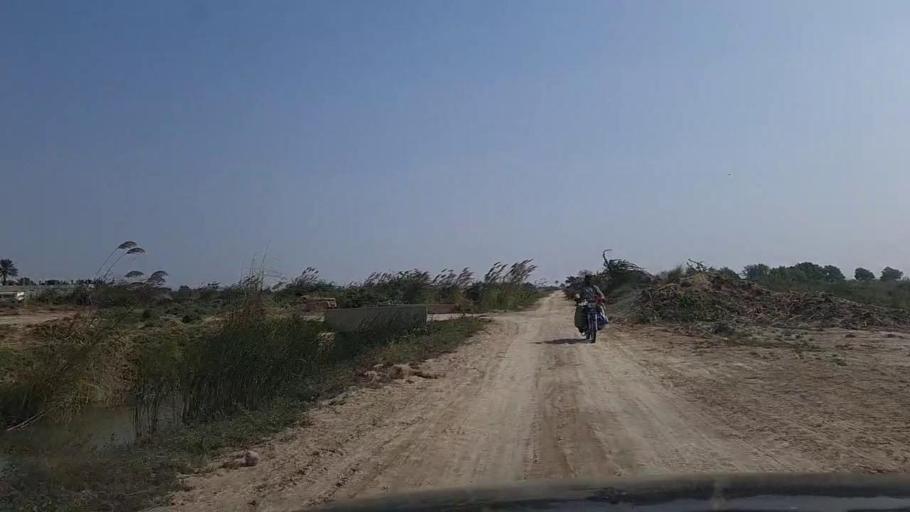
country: PK
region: Sindh
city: Gharo
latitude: 24.7159
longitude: 67.5704
